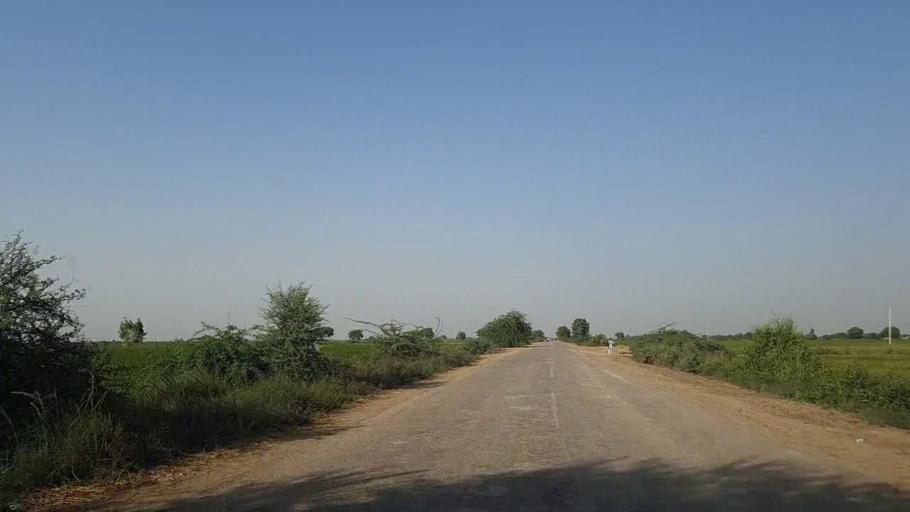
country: PK
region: Sindh
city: Mirpur Batoro
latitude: 24.5841
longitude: 68.3967
